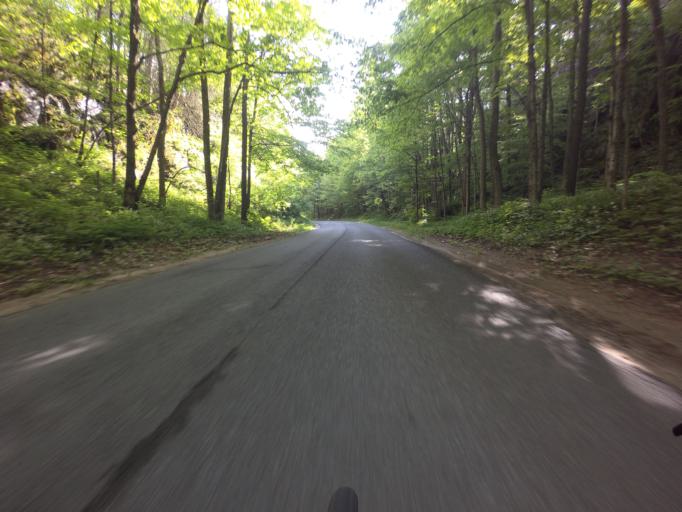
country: US
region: New York
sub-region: St. Lawrence County
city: Gouverneur
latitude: 44.2037
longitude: -75.2548
